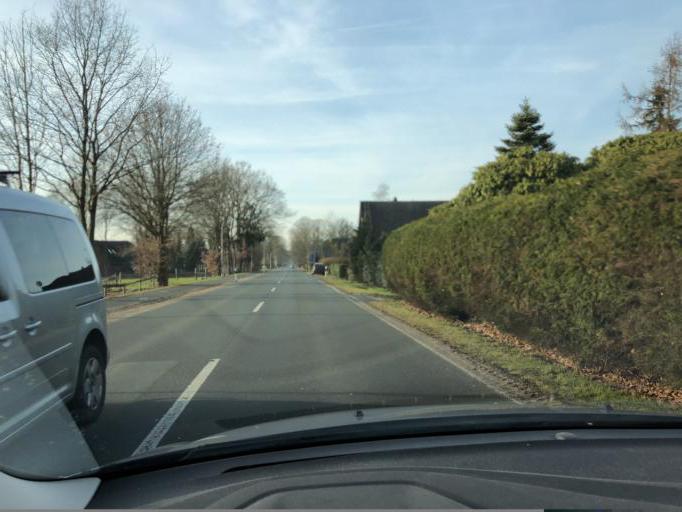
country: DE
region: Lower Saxony
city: Wiefelstede
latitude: 53.1420
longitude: 8.1017
